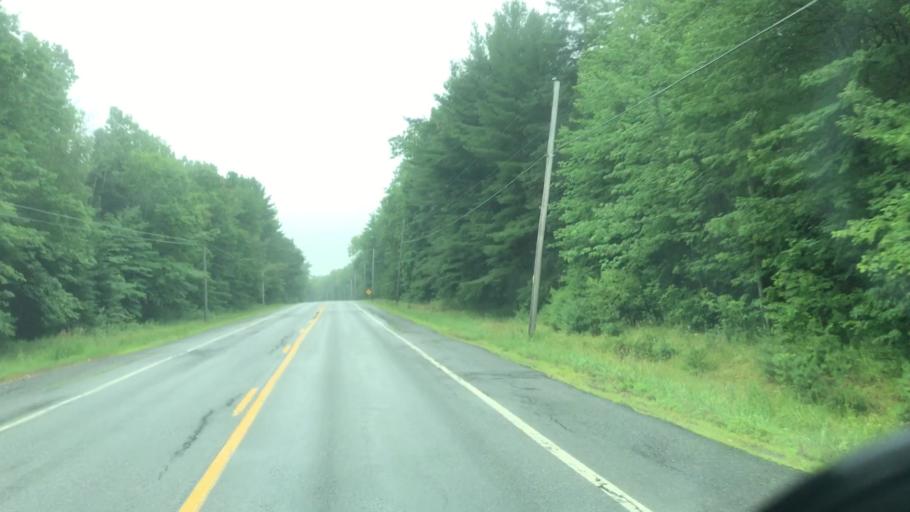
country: US
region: Maine
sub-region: Penobscot County
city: Howland
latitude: 45.2754
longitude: -68.6350
